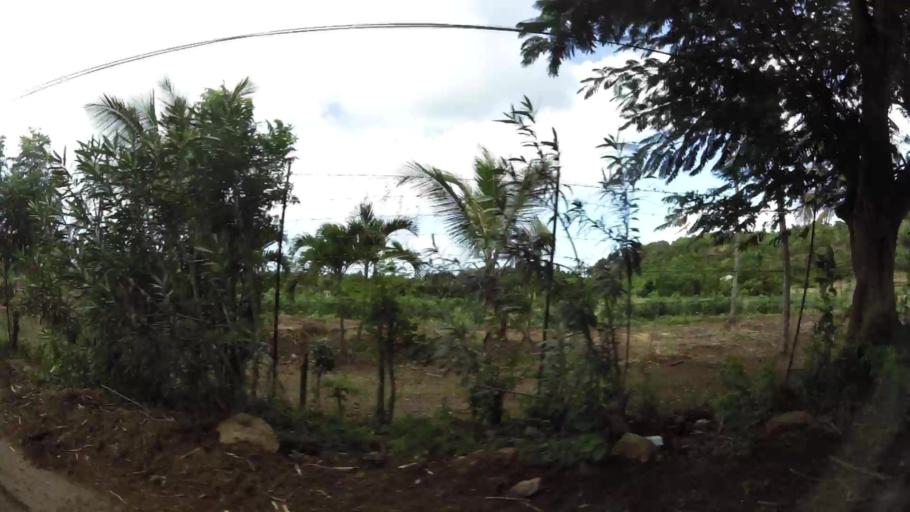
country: AG
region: Saint John
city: Saint John's
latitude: 17.1182
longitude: -61.8906
